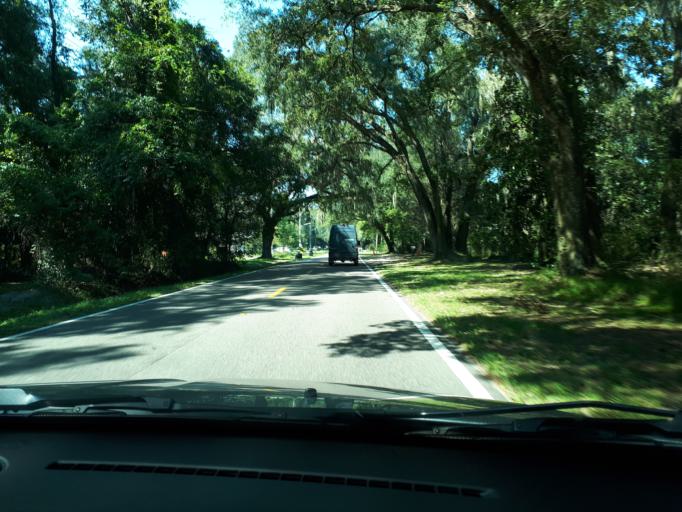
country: US
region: Florida
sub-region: Clay County
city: Bellair-Meadowbrook Terrace
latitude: 30.2780
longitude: -81.8318
